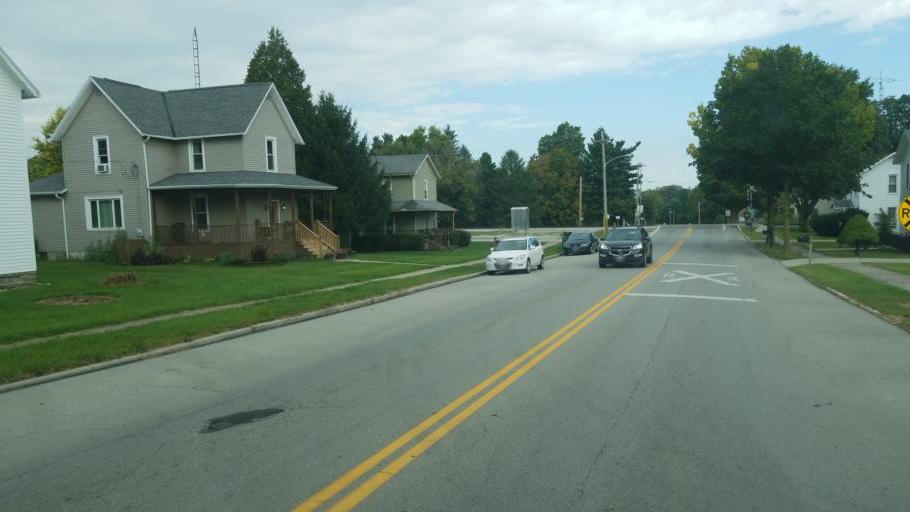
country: US
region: Ohio
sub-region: Seneca County
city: Tiffin
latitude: 40.9521
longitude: -83.1700
